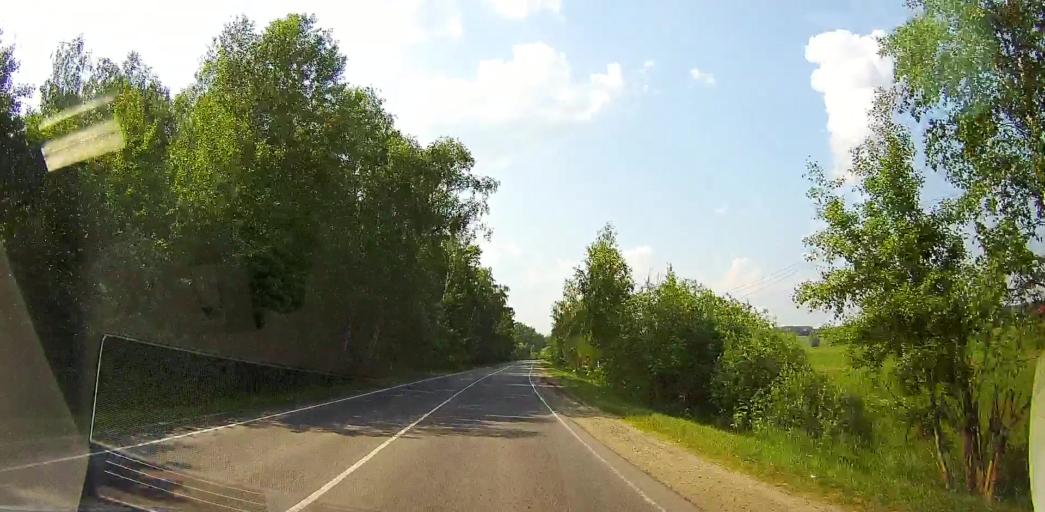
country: RU
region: Moskovskaya
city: Il'inskoye
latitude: 55.1998
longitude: 37.9672
